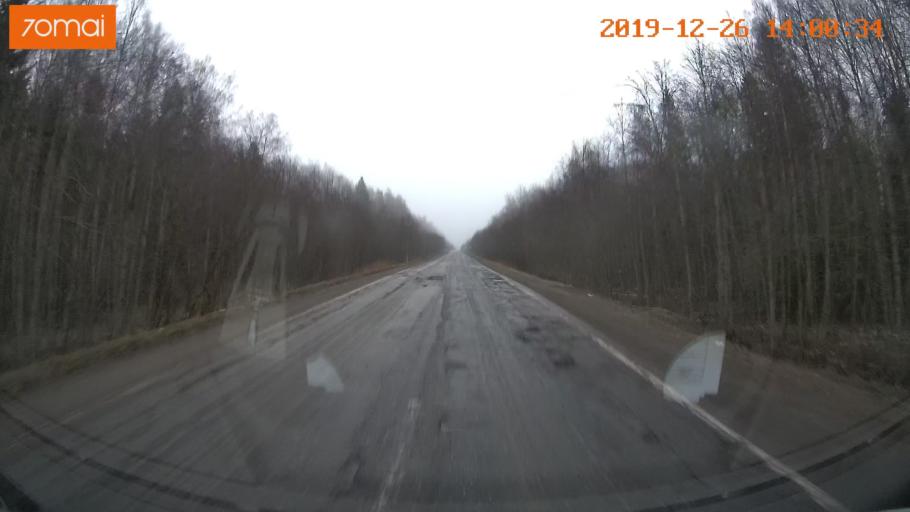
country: RU
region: Jaroslavl
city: Poshekhon'ye
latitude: 58.5571
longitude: 38.7461
